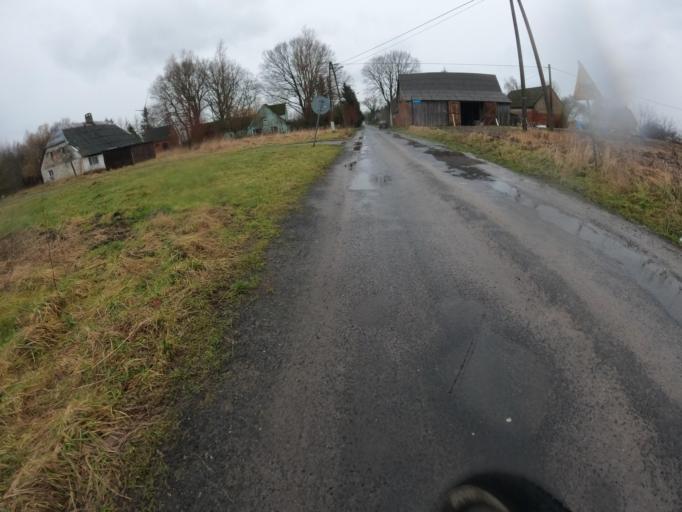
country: PL
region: West Pomeranian Voivodeship
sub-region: Powiat slawienski
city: Darlowo
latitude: 54.3932
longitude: 16.5260
